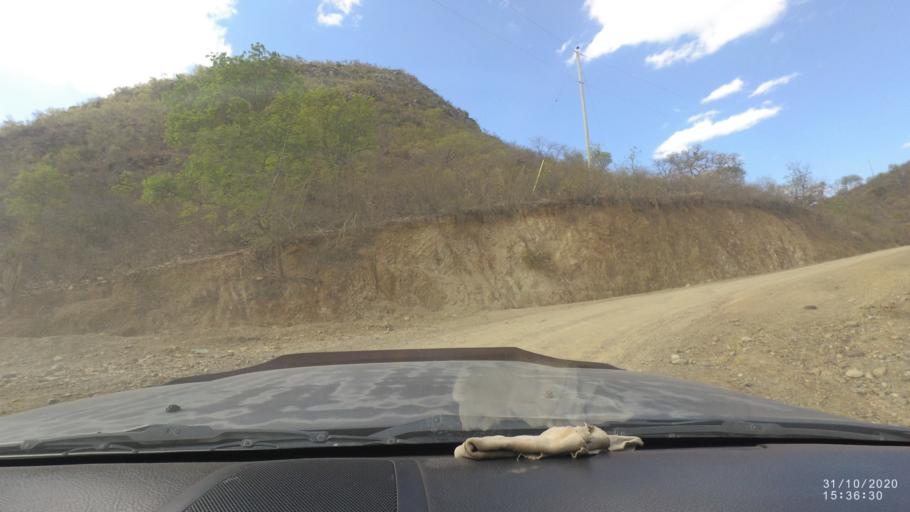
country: BO
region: Chuquisaca
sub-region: Provincia Zudanez
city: Mojocoya
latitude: -18.3409
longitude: -64.7534
